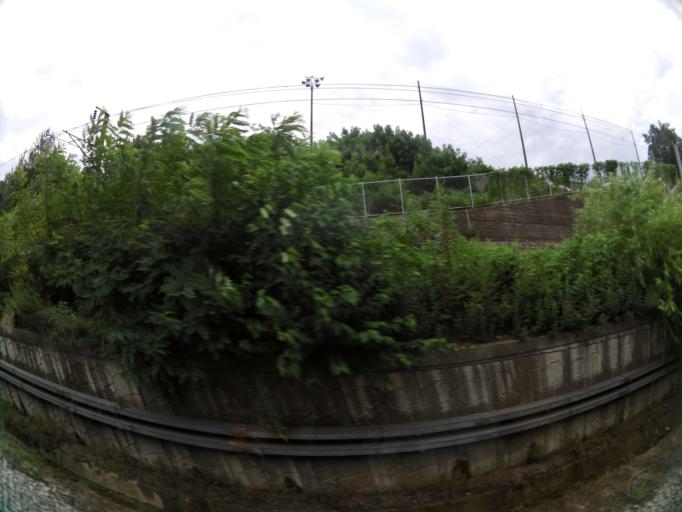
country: KR
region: Chungcheongnam-do
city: Cheonan
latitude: 36.8277
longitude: 127.1495
